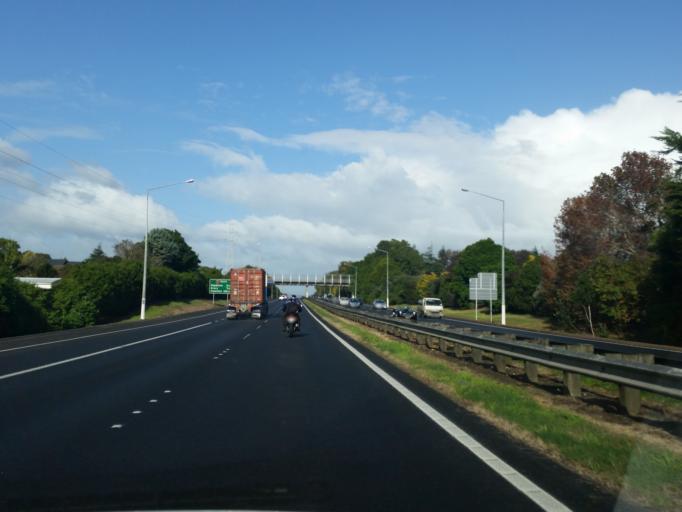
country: NZ
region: Auckland
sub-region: Auckland
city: Takanini
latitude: -37.0421
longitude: 174.9113
